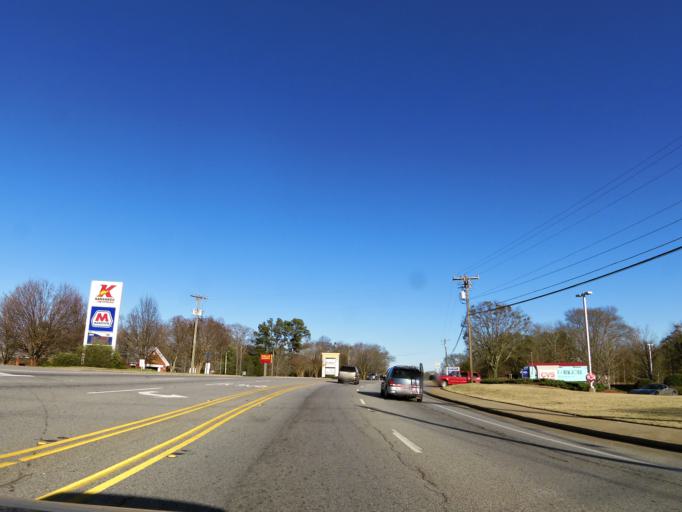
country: US
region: South Carolina
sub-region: Spartanburg County
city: Wellford
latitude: 34.8867
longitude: -82.0669
